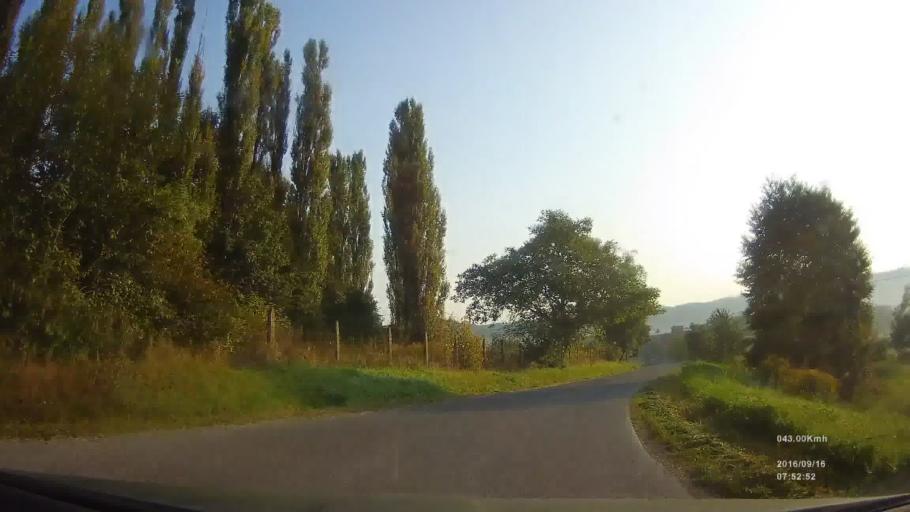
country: SK
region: Presovsky
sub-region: Okres Presov
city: Presov
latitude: 48.9181
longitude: 21.1026
